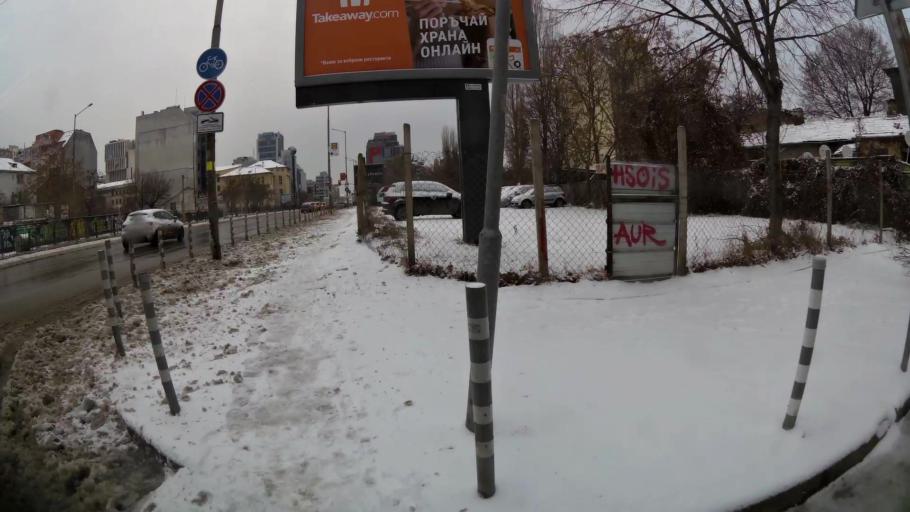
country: BG
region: Sofia-Capital
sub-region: Stolichna Obshtina
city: Sofia
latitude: 42.6997
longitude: 23.3119
